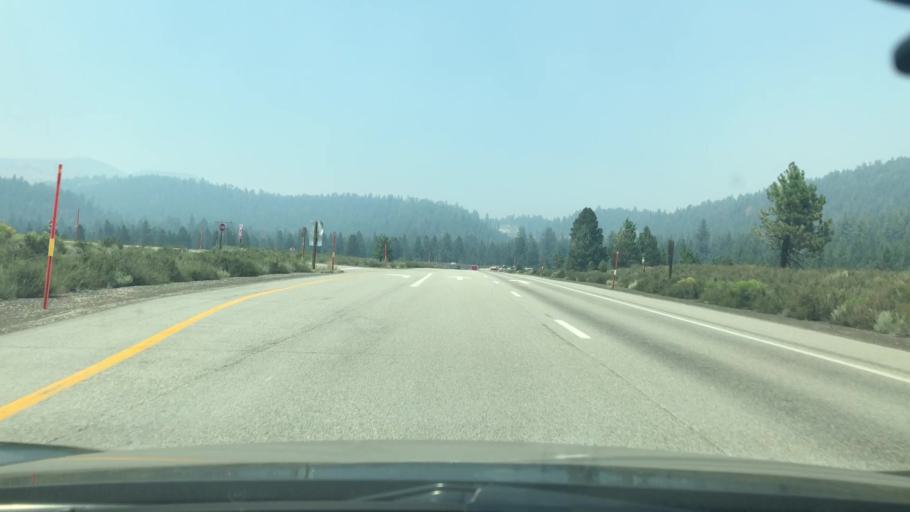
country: US
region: California
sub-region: Mono County
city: Mammoth Lakes
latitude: 37.7461
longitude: -118.9795
